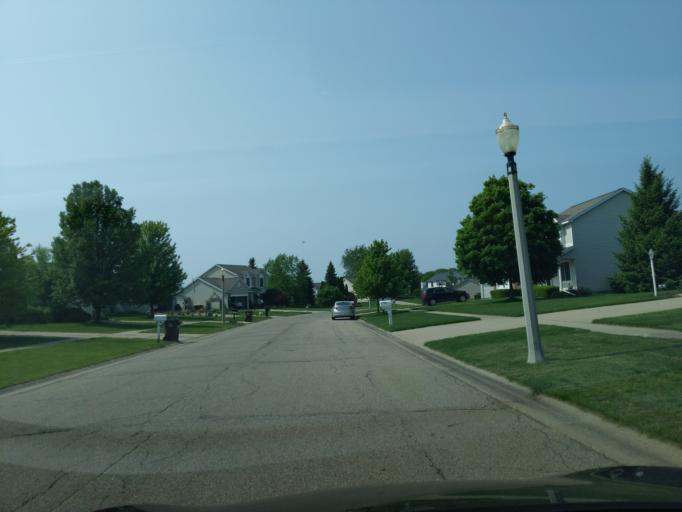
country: US
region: Michigan
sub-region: Eaton County
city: Waverly
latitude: 42.7491
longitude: -84.6548
